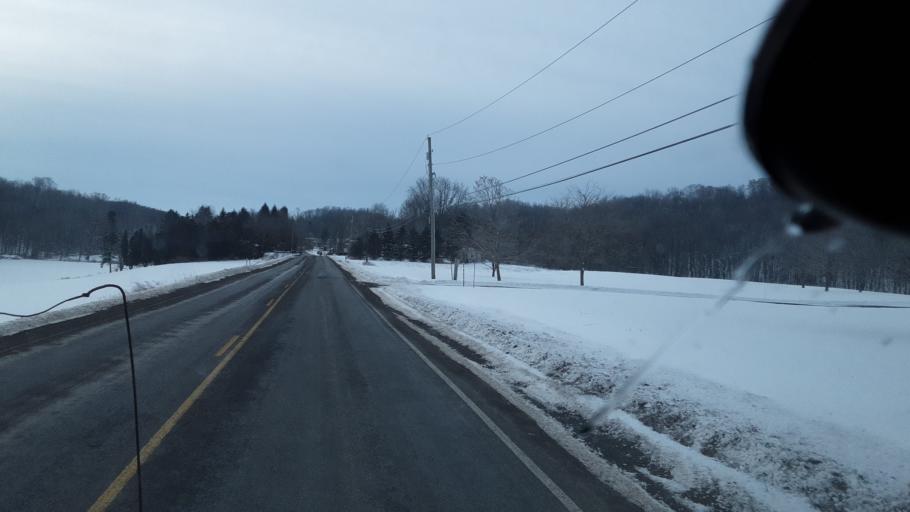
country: US
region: New York
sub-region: Wayne County
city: Lyons
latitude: 43.0810
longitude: -76.9963
